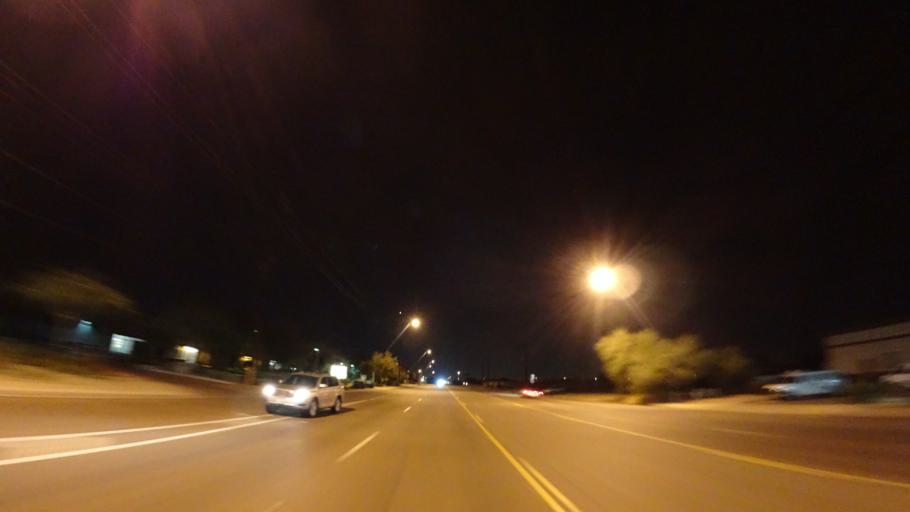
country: US
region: Arizona
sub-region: Pinal County
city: Apache Junction
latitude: 33.3933
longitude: -111.6341
